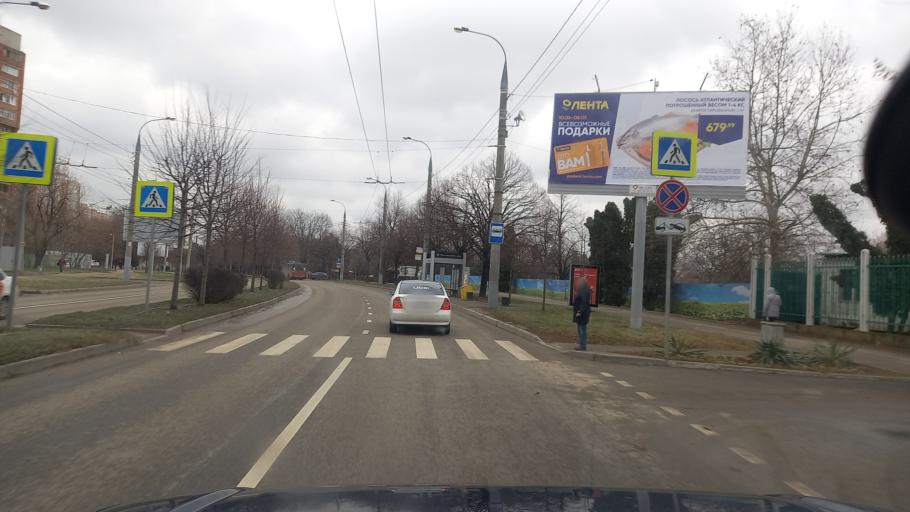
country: RU
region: Krasnodarskiy
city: Pashkovskiy
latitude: 45.0331
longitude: 39.0998
